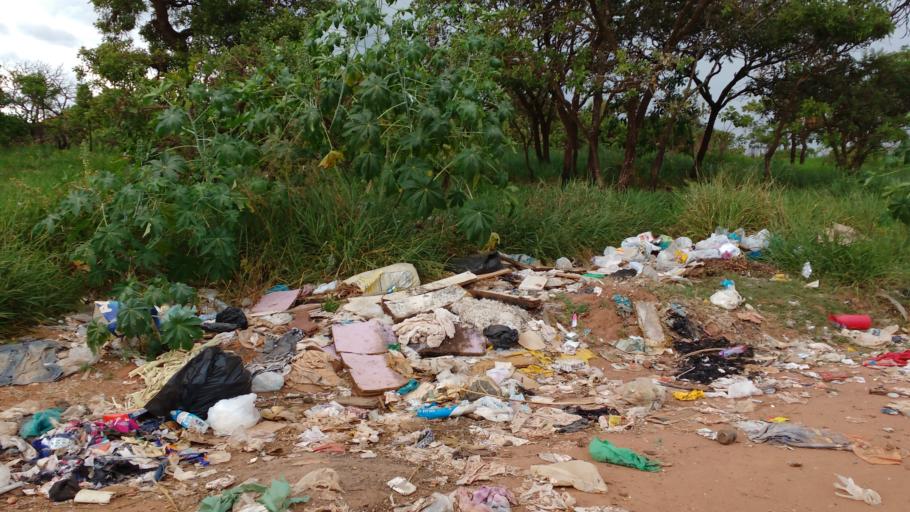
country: BR
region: Sao Paulo
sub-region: Casa Branca
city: Casa Branca
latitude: -21.7592
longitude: -47.0821
